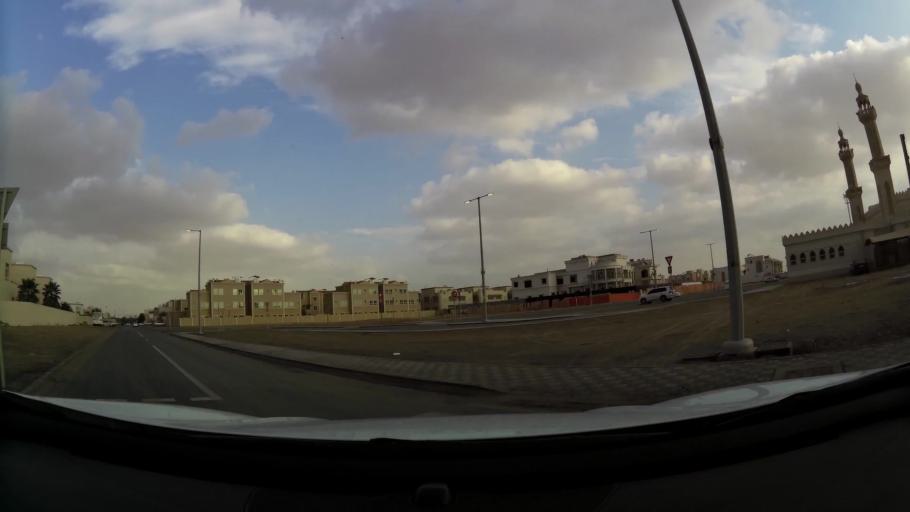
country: AE
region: Abu Dhabi
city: Abu Dhabi
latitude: 24.3544
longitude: 54.5585
